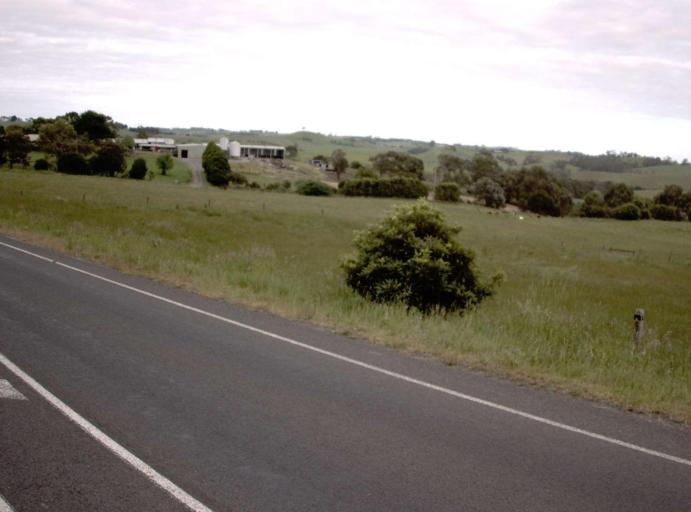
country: AU
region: Victoria
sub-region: Bass Coast
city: North Wonthaggi
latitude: -38.4433
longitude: 145.8054
